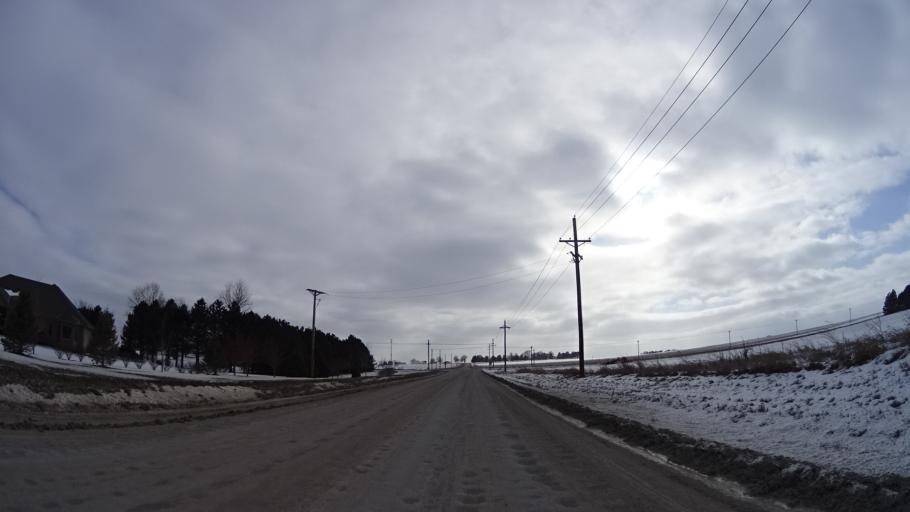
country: US
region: Nebraska
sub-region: Sarpy County
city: Papillion
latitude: 41.1196
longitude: -96.0237
